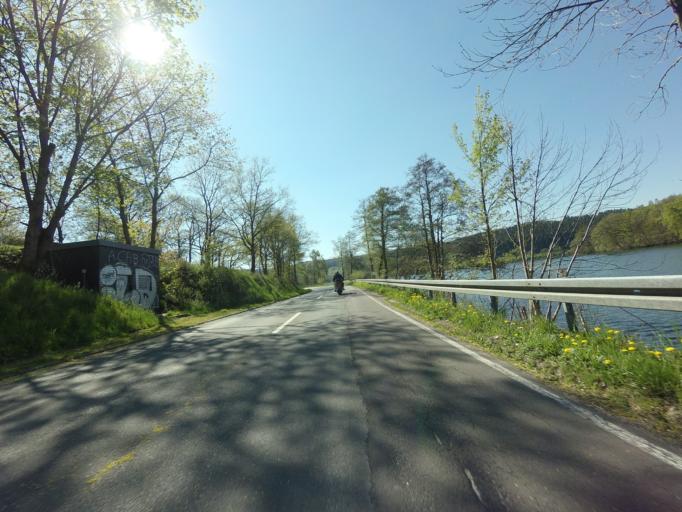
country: DE
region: North Rhine-Westphalia
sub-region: Regierungsbezirk Arnsberg
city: Drolshagen
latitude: 51.0773
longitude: 7.8029
